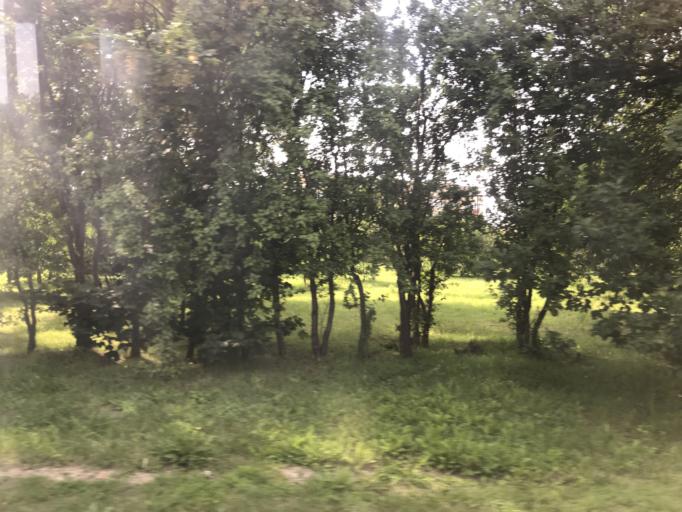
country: PL
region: Pomeranian Voivodeship
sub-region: Gdansk
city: Gdansk
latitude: 54.4024
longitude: 18.6308
